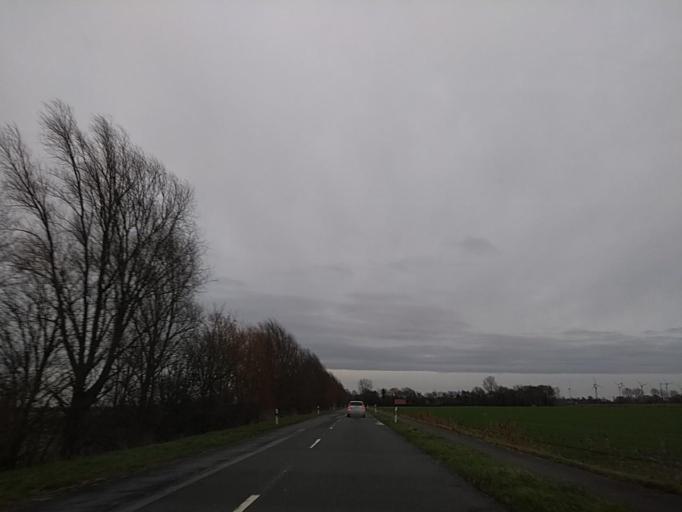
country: DE
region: Lower Saxony
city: Hinte
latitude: 53.3526
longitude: 7.0837
